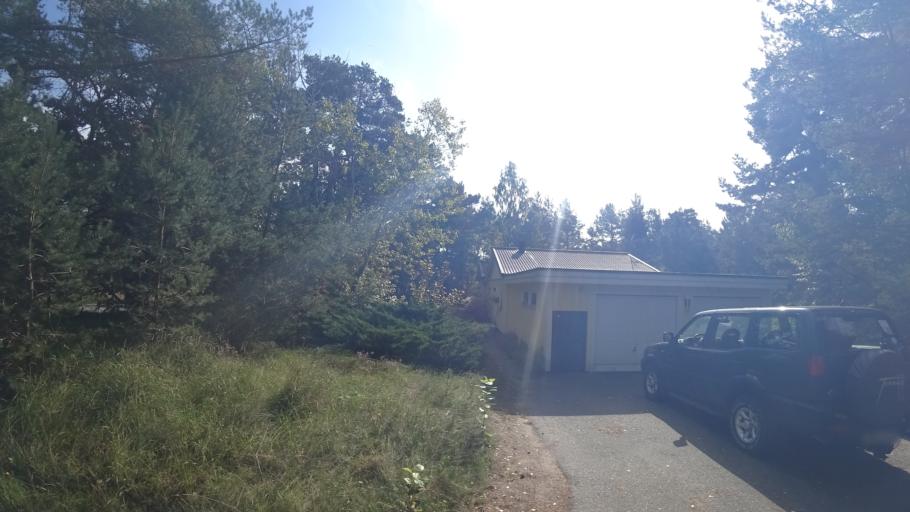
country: SE
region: Skane
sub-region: Kristianstads Kommun
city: Ahus
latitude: 55.9089
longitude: 14.2900
